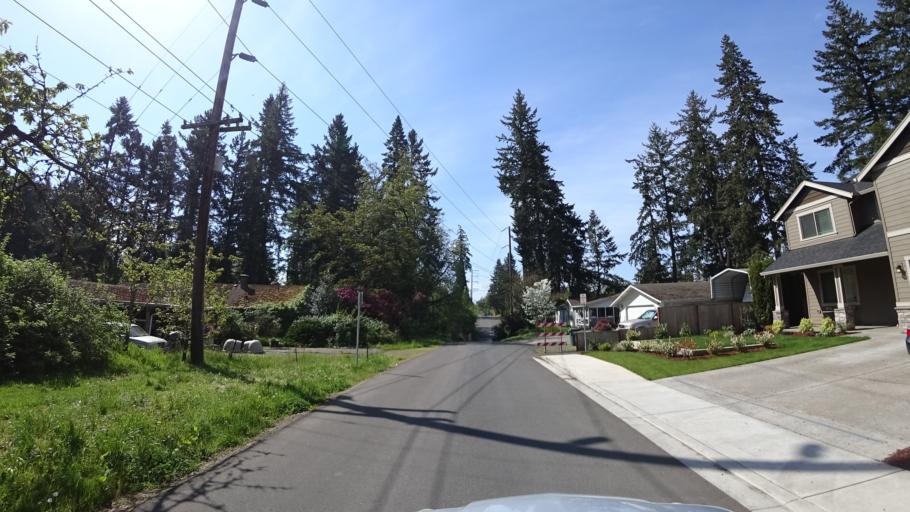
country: US
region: Oregon
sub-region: Washington County
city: Hillsboro
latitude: 45.5250
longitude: -122.9379
